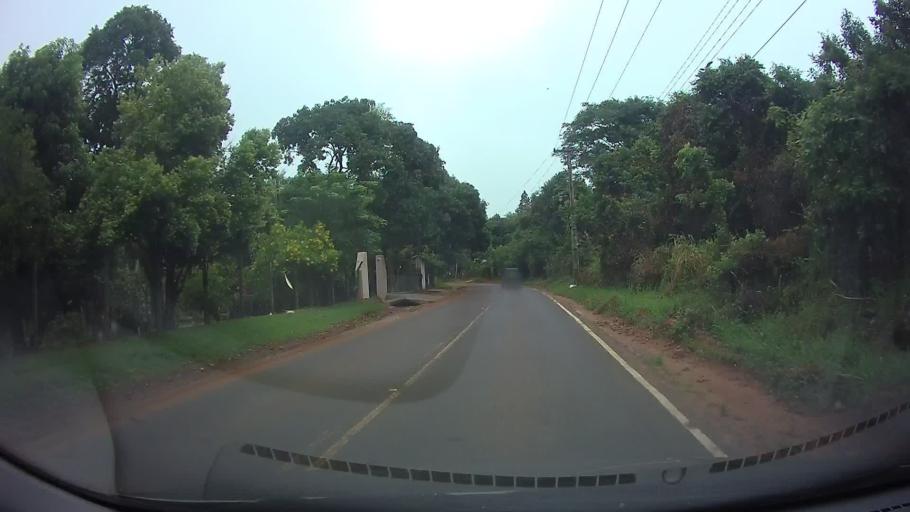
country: PY
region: Central
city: Itaugua
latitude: -25.3576
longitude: -57.3445
